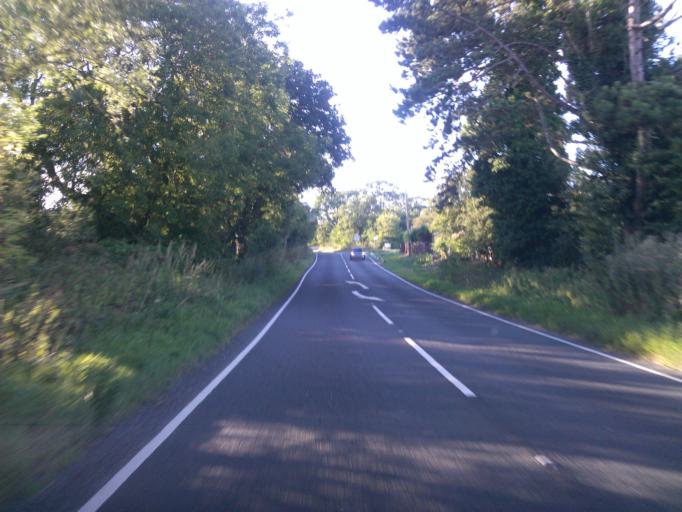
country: GB
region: England
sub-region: Essex
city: Saint Osyth
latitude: 51.8214
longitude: 1.0696
